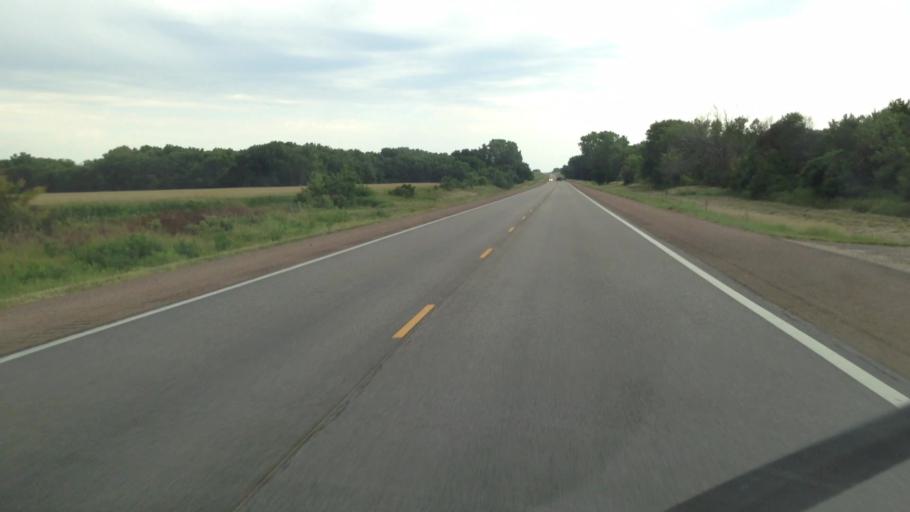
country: US
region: Kansas
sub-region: Woodson County
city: Yates Center
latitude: 38.0322
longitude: -95.7390
